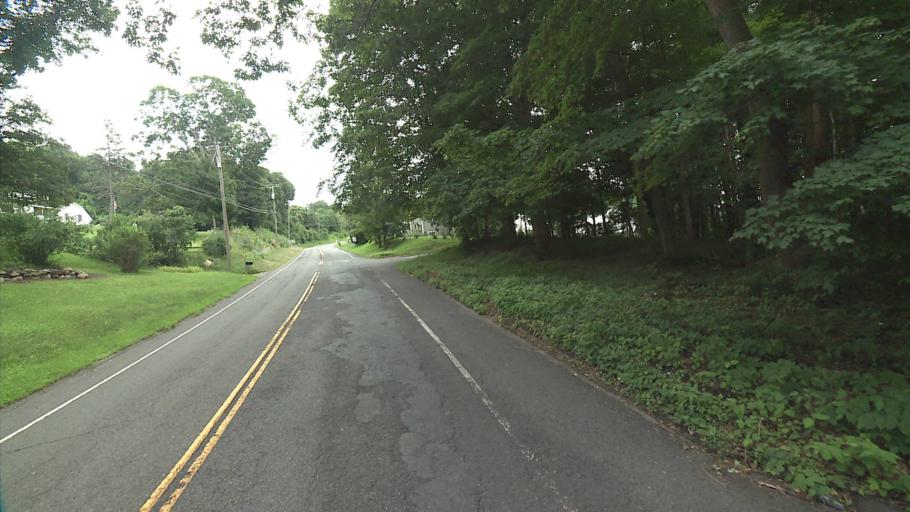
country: US
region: Connecticut
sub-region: Litchfield County
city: New Milford
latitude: 41.5702
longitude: -73.4015
